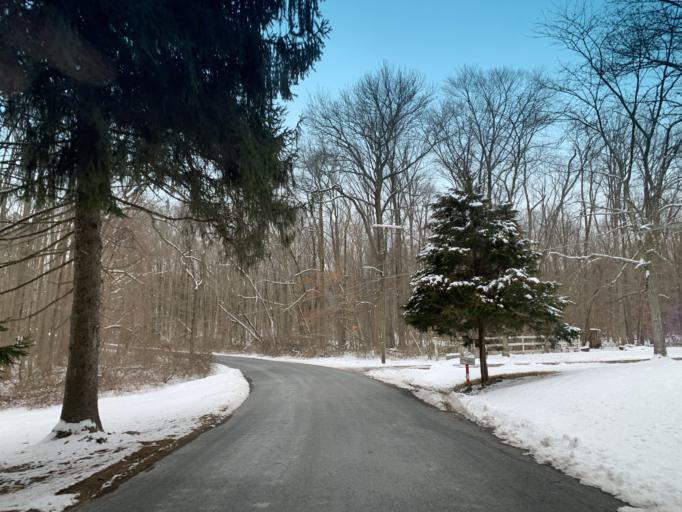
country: US
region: Maryland
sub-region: Harford County
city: Aberdeen
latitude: 39.5630
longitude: -76.1831
